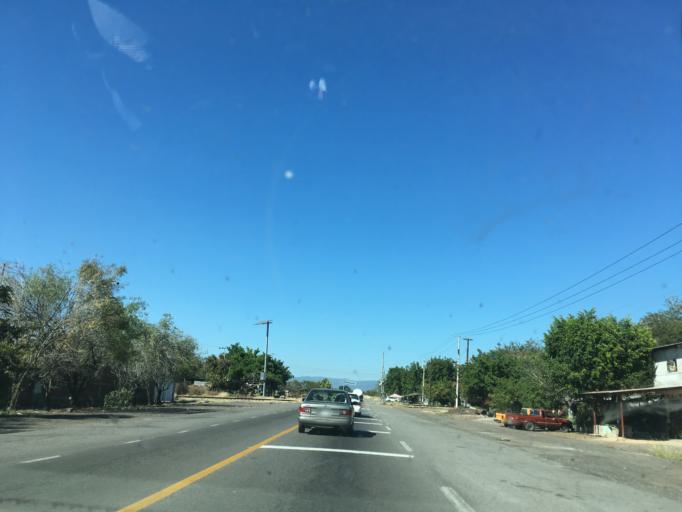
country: MX
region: Michoacan
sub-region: Gabriel Zamora
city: Lombardia
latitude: 19.0959
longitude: -102.0578
